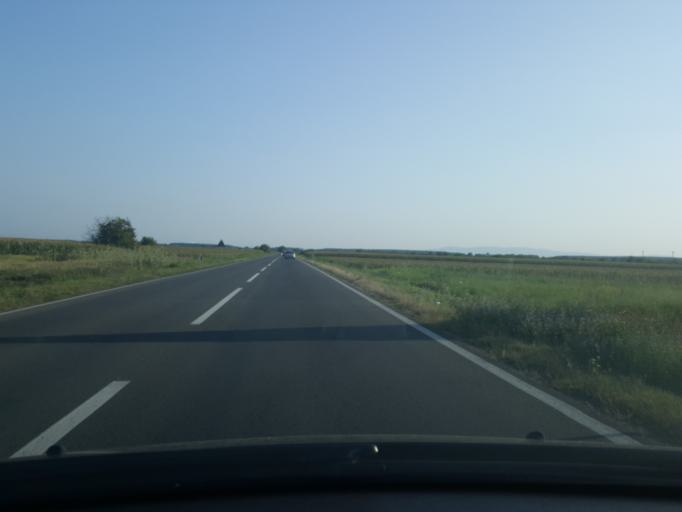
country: RS
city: Klenak
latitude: 44.7965
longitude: 19.7284
